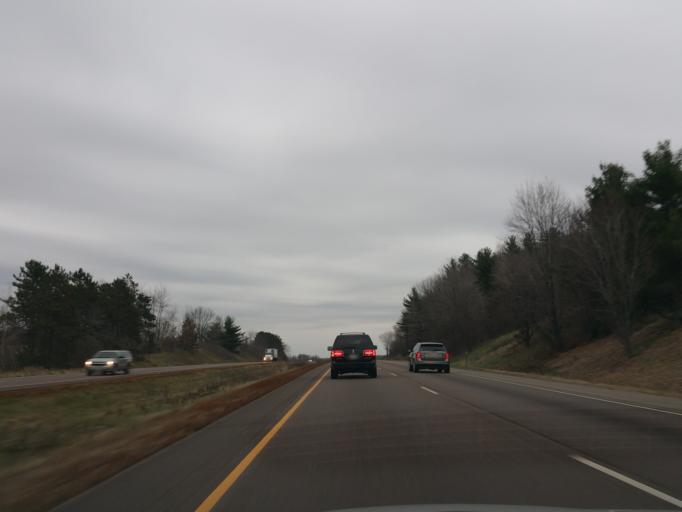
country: US
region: Wisconsin
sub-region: Dunn County
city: Menomonie
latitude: 44.9169
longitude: -92.0025
